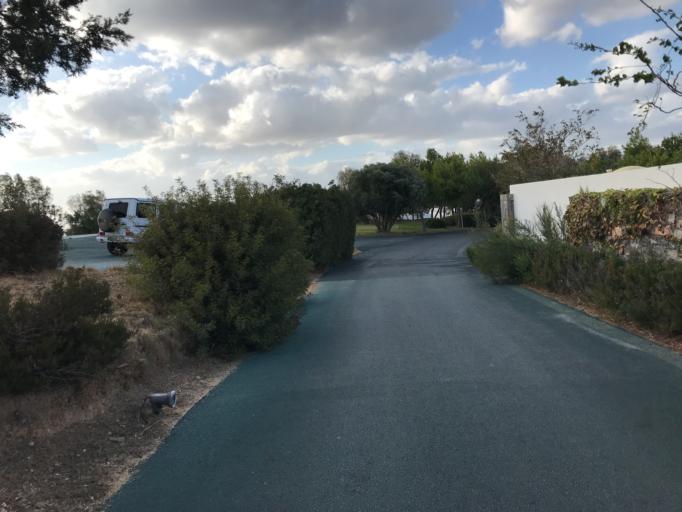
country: GR
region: Attica
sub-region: Nomarchia Anatolikis Attikis
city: Saronida
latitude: 37.7759
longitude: 23.8879
